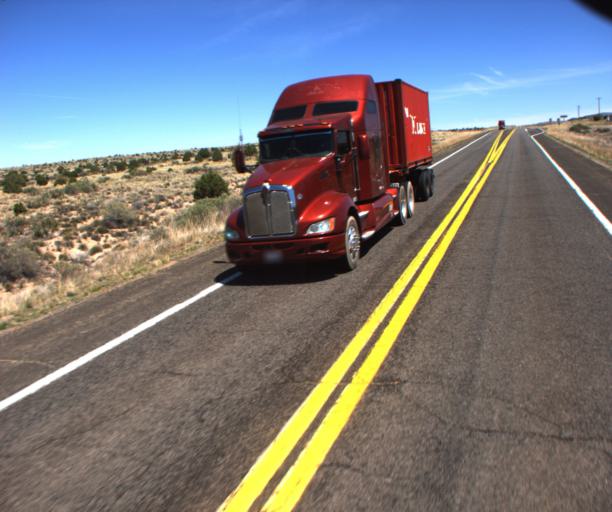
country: US
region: Arizona
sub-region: Mohave County
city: Peach Springs
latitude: 35.5006
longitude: -113.5308
